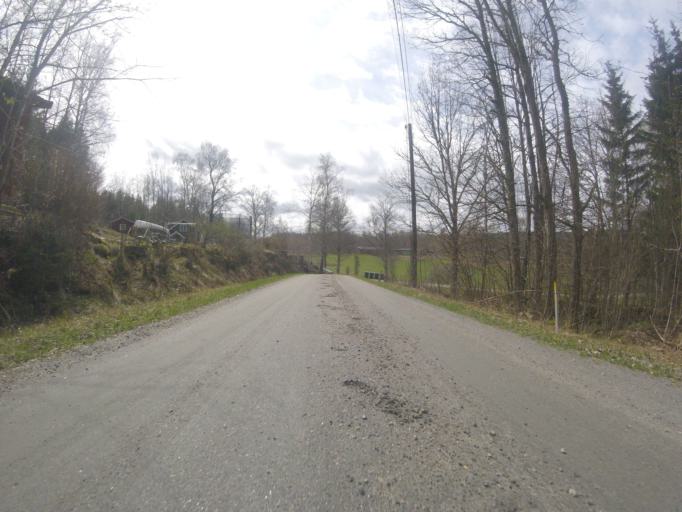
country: SE
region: Vaestra Goetaland
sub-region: Alingsas Kommun
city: Ingared
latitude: 57.8673
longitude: 12.5043
